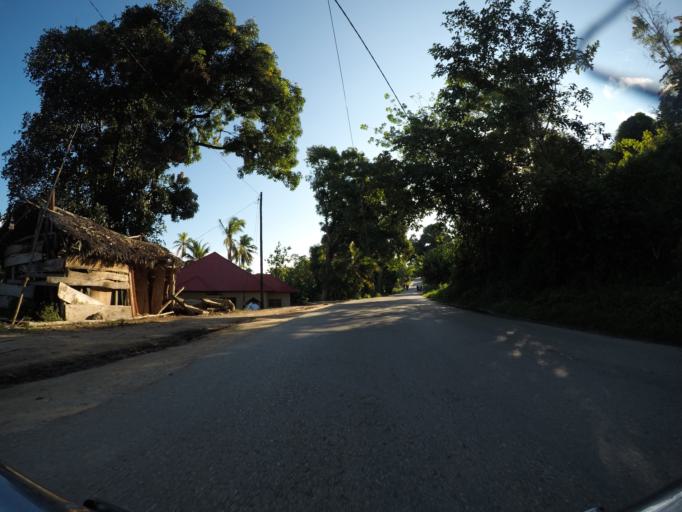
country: TZ
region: Pemba South
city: Mtambile
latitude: -5.3207
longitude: 39.7421
